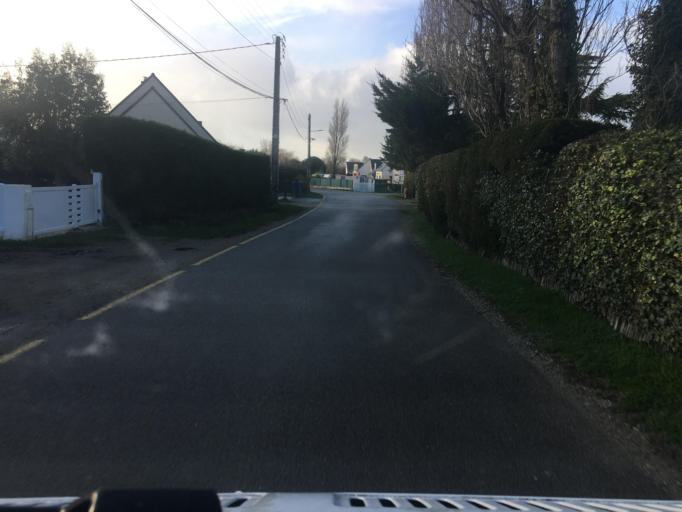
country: FR
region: Brittany
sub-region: Departement du Morbihan
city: Sarzeau
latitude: 47.4989
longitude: -2.6843
